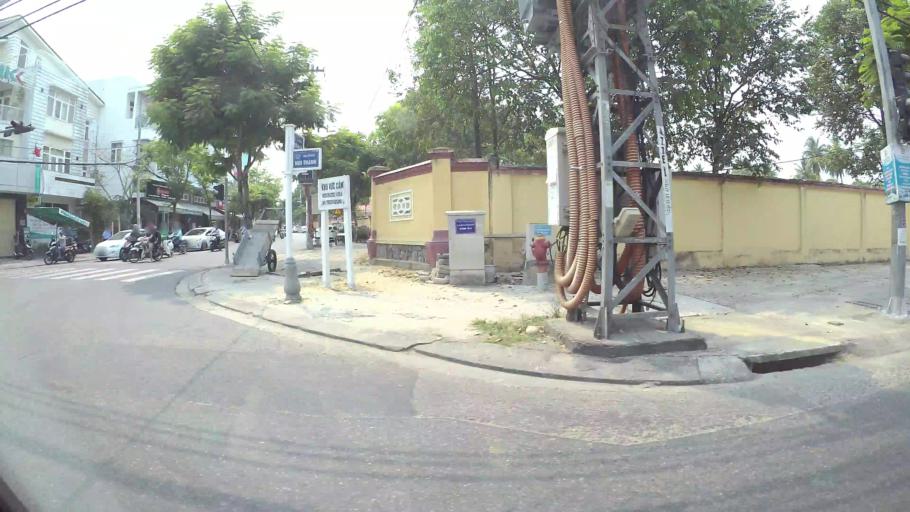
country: VN
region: Da Nang
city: Son Tra
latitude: 16.0467
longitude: 108.2211
